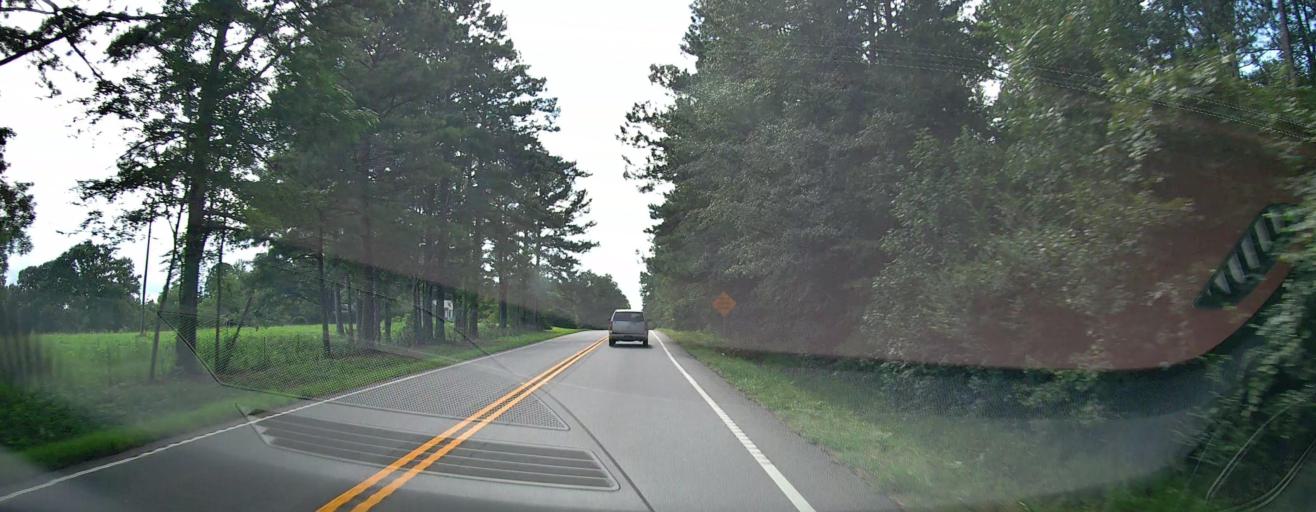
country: US
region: Georgia
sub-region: Meriwether County
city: Manchester
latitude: 32.9854
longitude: -84.5466
